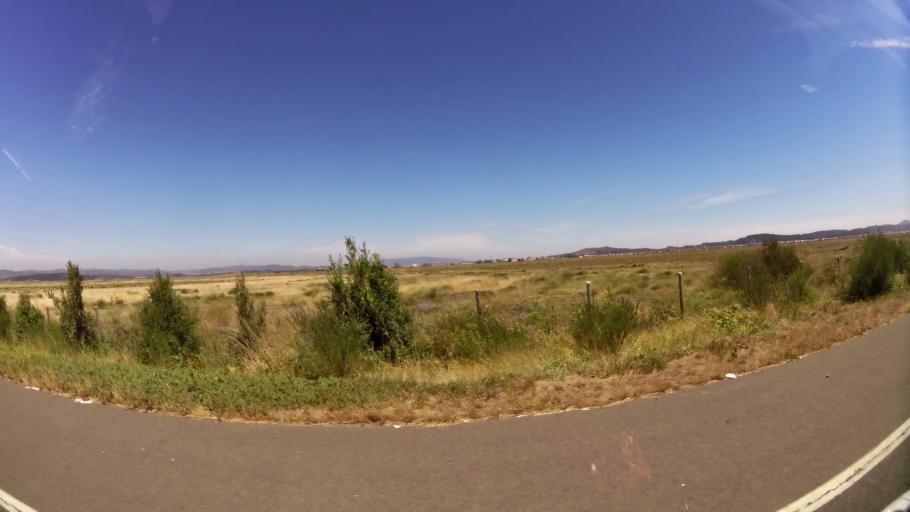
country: CL
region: Biobio
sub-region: Provincia de Concepcion
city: Talcahuano
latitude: -36.7336
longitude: -73.0695
